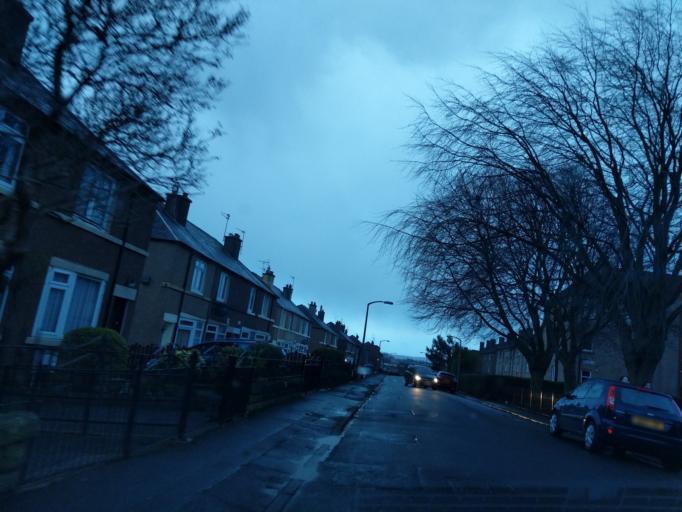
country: GB
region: Scotland
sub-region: West Lothian
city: Seafield
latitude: 55.9519
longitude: -3.1364
